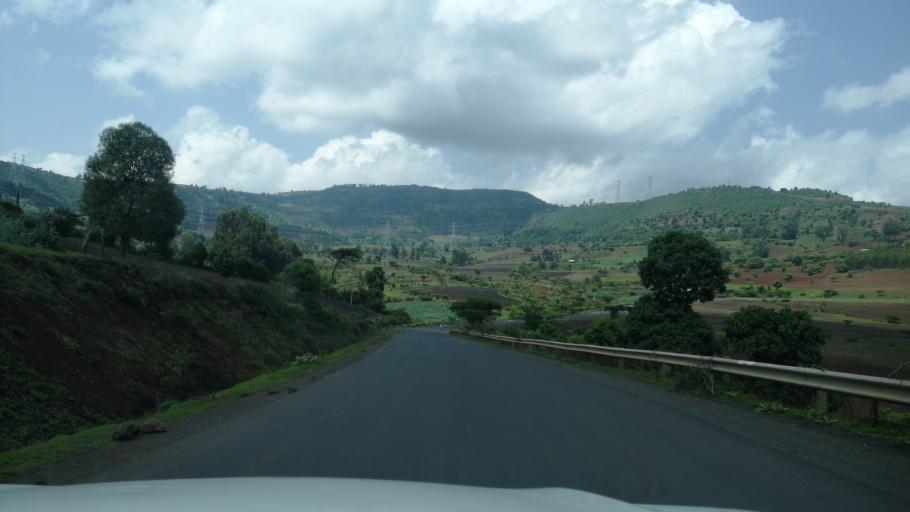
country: ET
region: Oromiya
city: Gedo
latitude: 8.9819
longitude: 37.6034
